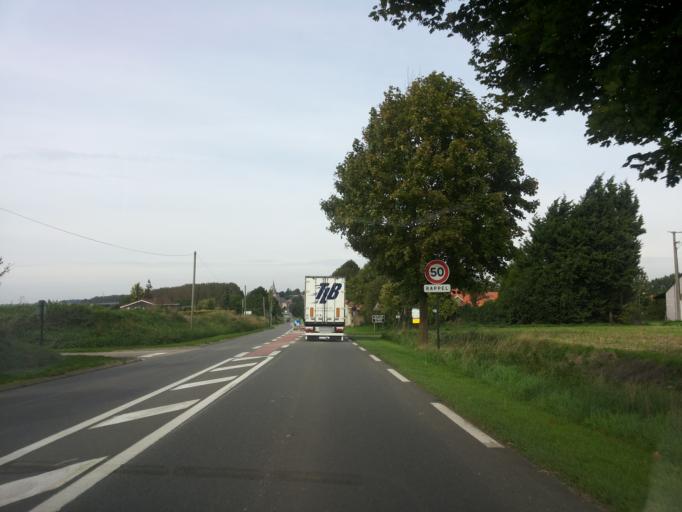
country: FR
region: Nord-Pas-de-Calais
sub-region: Departement du Pas-de-Calais
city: Biache-Saint-Vaast
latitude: 50.2448
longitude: 2.9536
